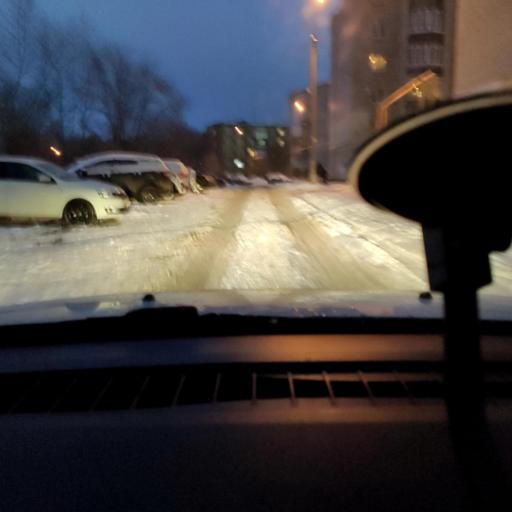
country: RU
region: Samara
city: Rozhdestveno
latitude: 53.1419
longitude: 50.0469
